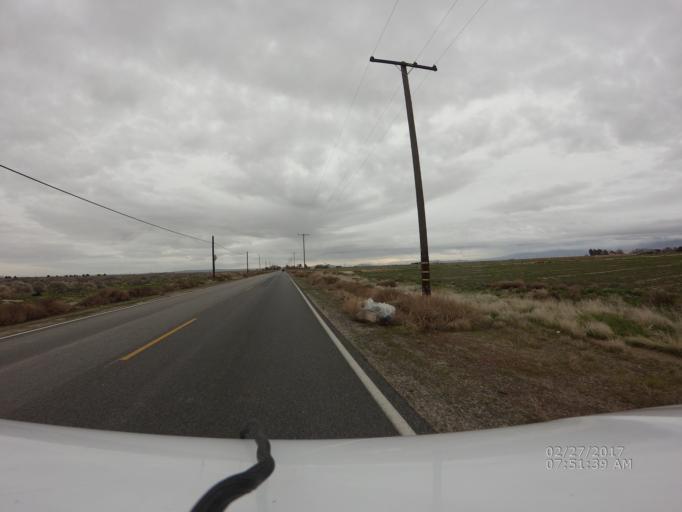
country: US
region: California
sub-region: Los Angeles County
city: Lancaster
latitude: 34.7045
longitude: -118.0488
